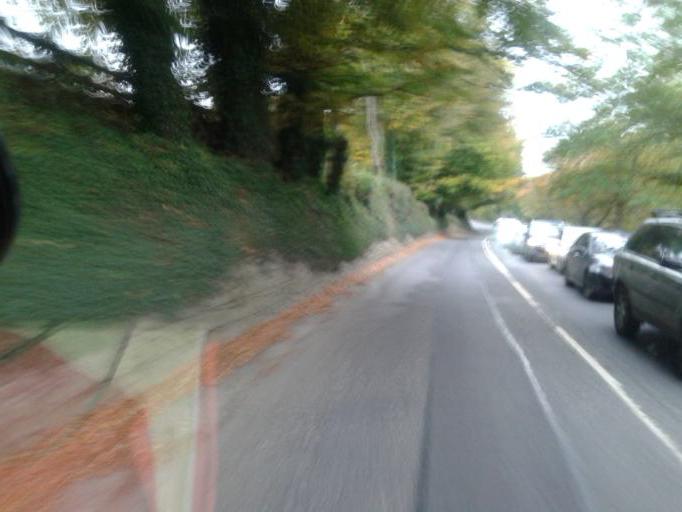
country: IE
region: Munster
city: Ballina
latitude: 52.8047
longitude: -8.4346
